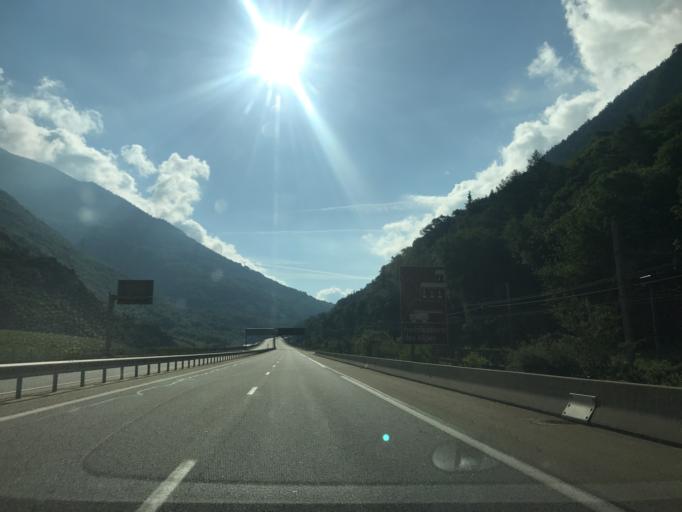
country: FR
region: Rhone-Alpes
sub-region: Departement de la Savoie
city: Saint-Michel-de-Maurienne
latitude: 45.2104
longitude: 6.4943
